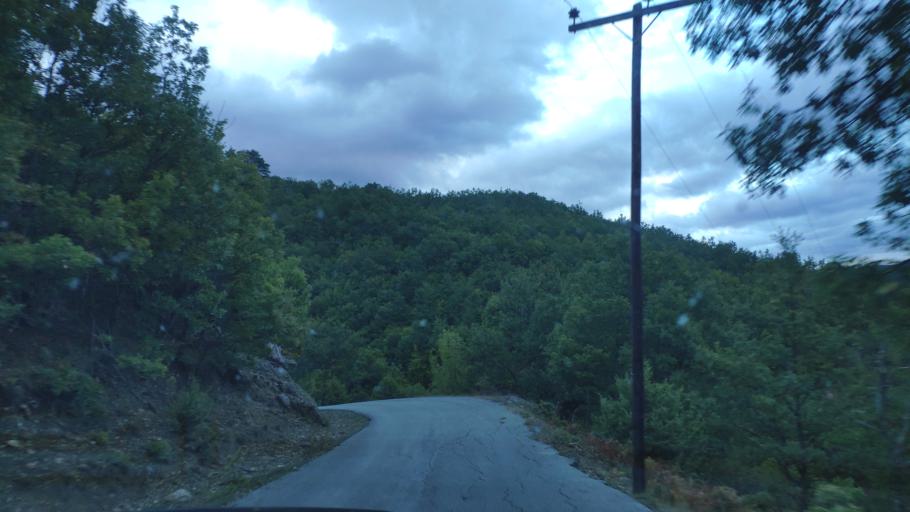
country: AL
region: Korce
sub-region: Rrethi i Kolonjes
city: Erseke
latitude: 40.2543
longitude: 20.8638
